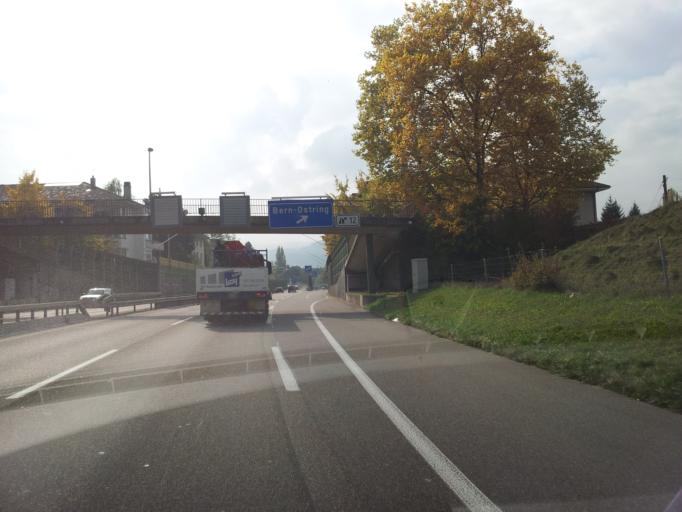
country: CH
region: Bern
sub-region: Bern-Mittelland District
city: Muri
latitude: 46.9485
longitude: 7.4732
